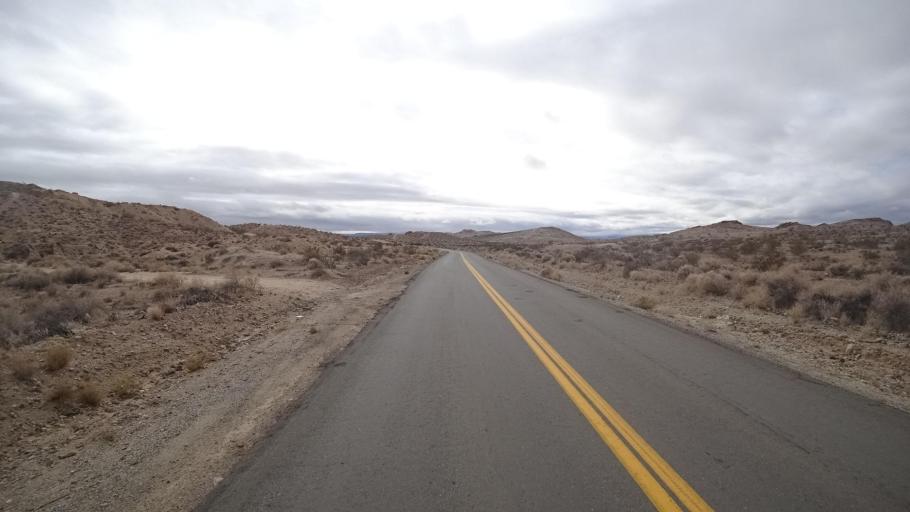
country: US
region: California
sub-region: Kern County
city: Rosamond
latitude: 34.9151
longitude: -118.2150
